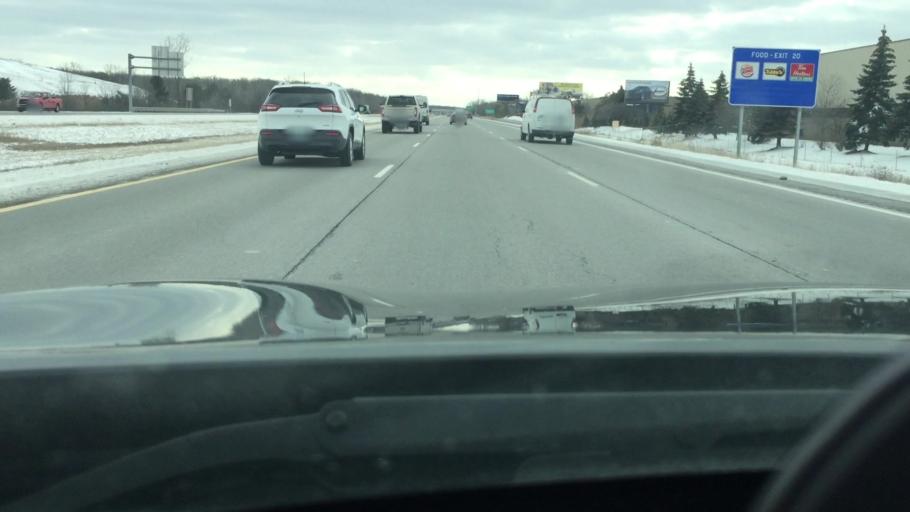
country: US
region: Michigan
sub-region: Wayne County
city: Wayne
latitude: 42.2614
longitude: -83.4409
